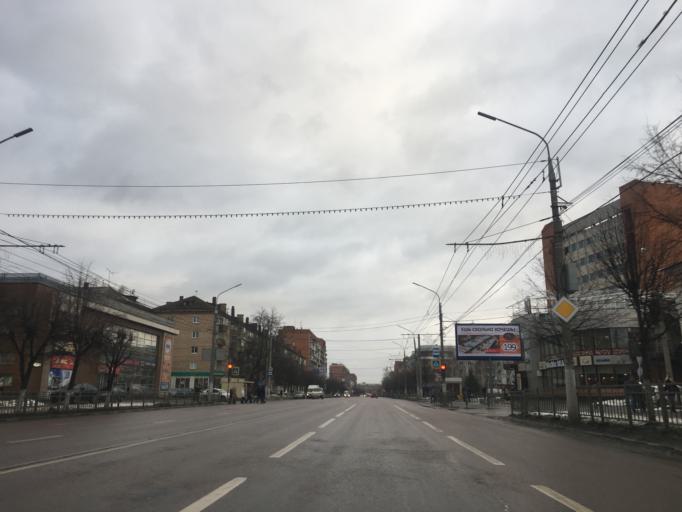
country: RU
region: Tula
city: Tula
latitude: 54.1975
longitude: 37.5946
